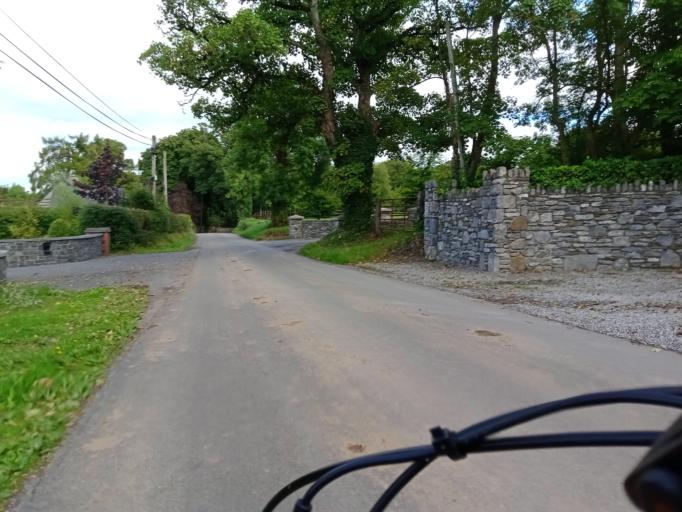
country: IE
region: Leinster
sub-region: Kilkenny
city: Kilkenny
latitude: 52.6154
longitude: -7.2049
